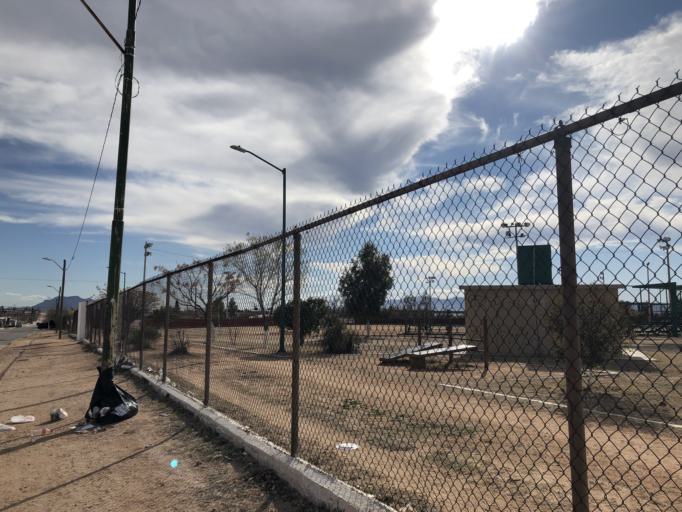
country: MX
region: Sonora
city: Agua Prieta
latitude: 31.3290
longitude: -109.5241
